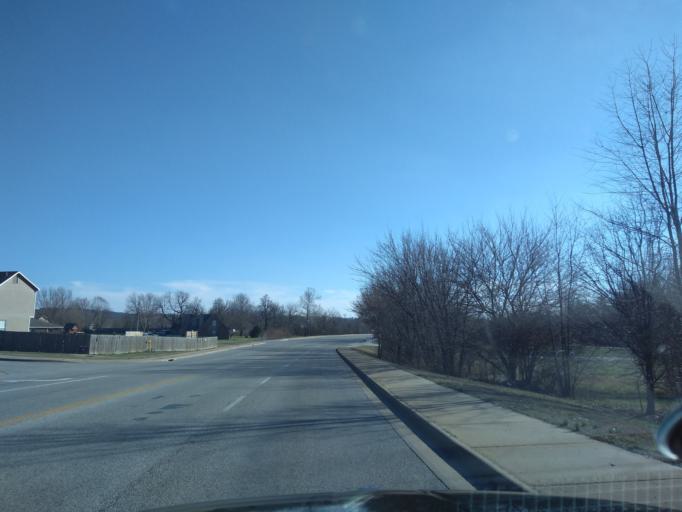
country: US
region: Arkansas
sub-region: Washington County
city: Johnson
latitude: 36.1251
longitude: -94.1623
